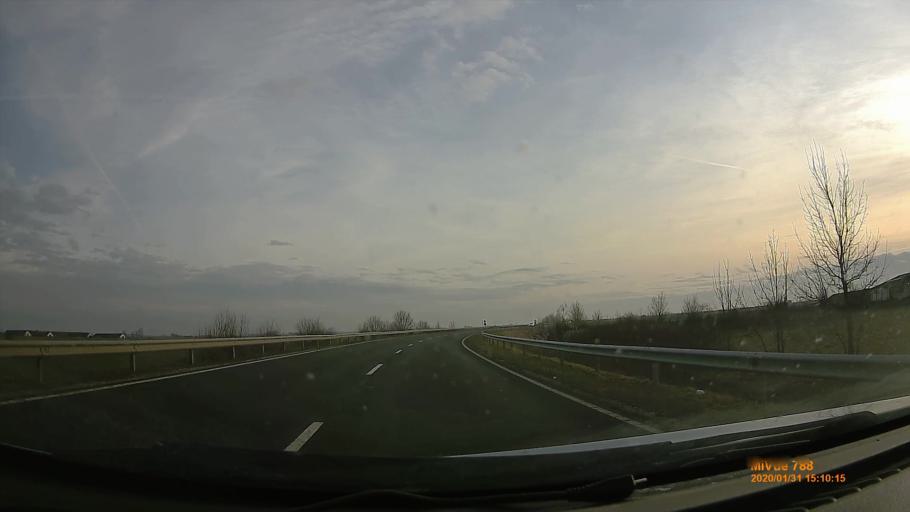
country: HU
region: Hajdu-Bihar
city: Polgar
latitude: 47.8642
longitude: 21.1527
